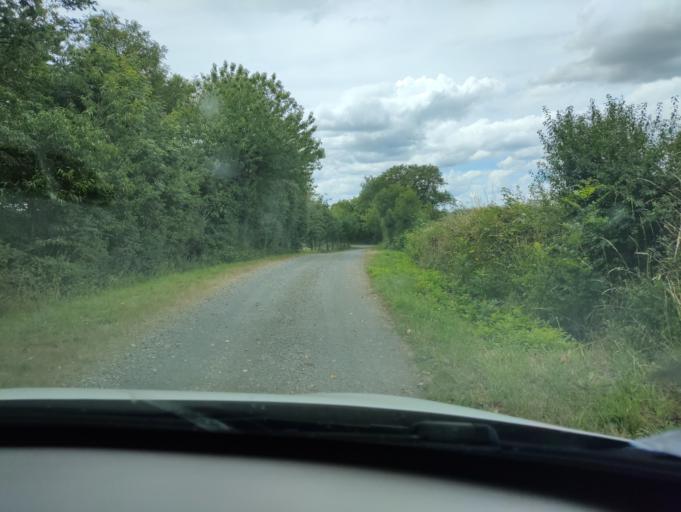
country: FR
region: Pays de la Loire
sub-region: Departement de la Loire-Atlantique
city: Chateaubriant
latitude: 47.7012
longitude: -1.4203
